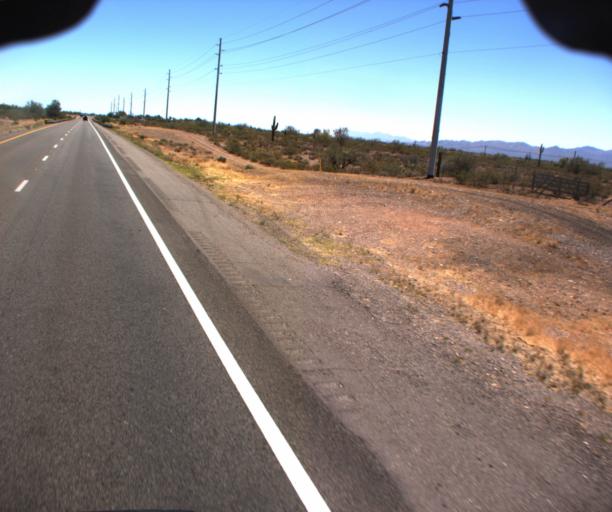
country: US
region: Arizona
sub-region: Maricopa County
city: Wickenburg
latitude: 33.8317
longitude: -112.5990
